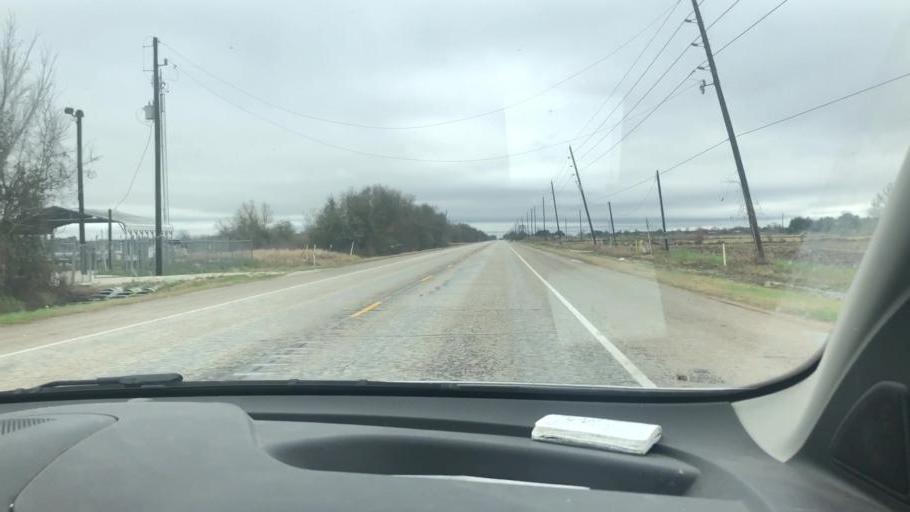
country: US
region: Texas
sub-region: Wharton County
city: Wharton
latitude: 29.2787
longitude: -96.0651
